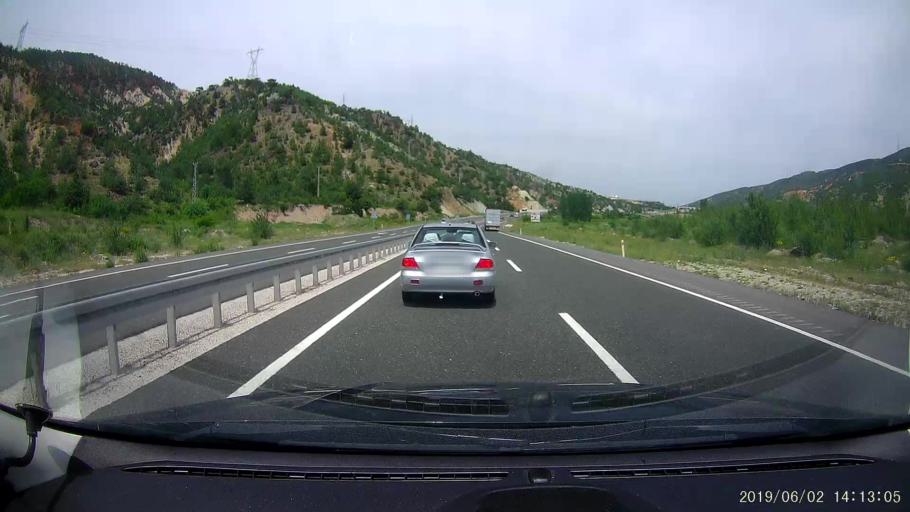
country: TR
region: Cankiri
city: Yaprakli
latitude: 40.9228
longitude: 33.8214
